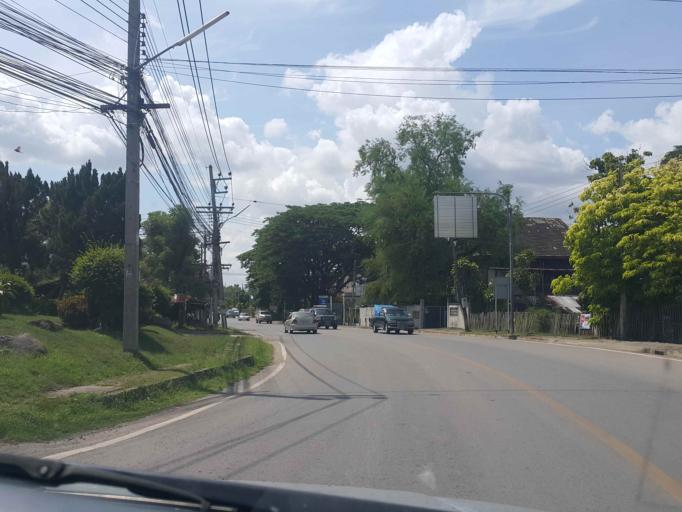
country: TH
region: Phayao
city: Phayao
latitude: 19.1656
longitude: 99.9082
